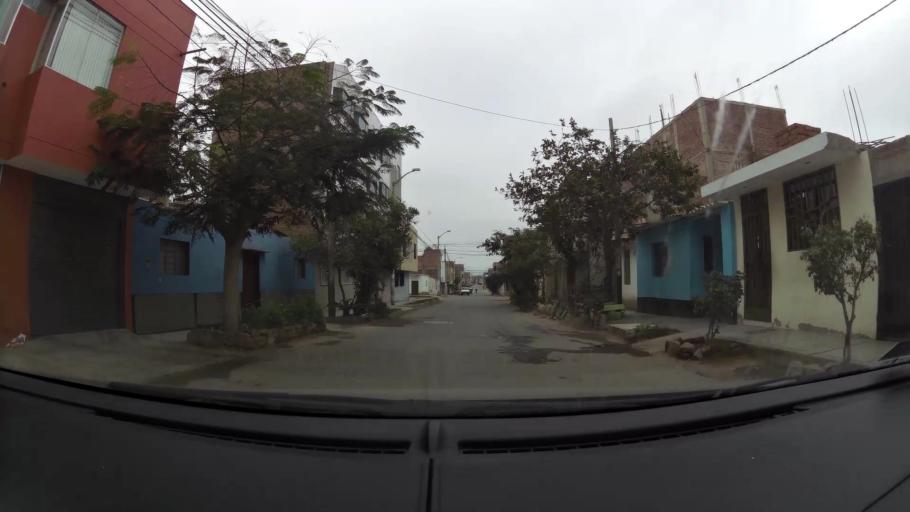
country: PE
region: La Libertad
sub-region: Provincia de Trujillo
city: La Esperanza
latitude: -8.0792
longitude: -79.0497
